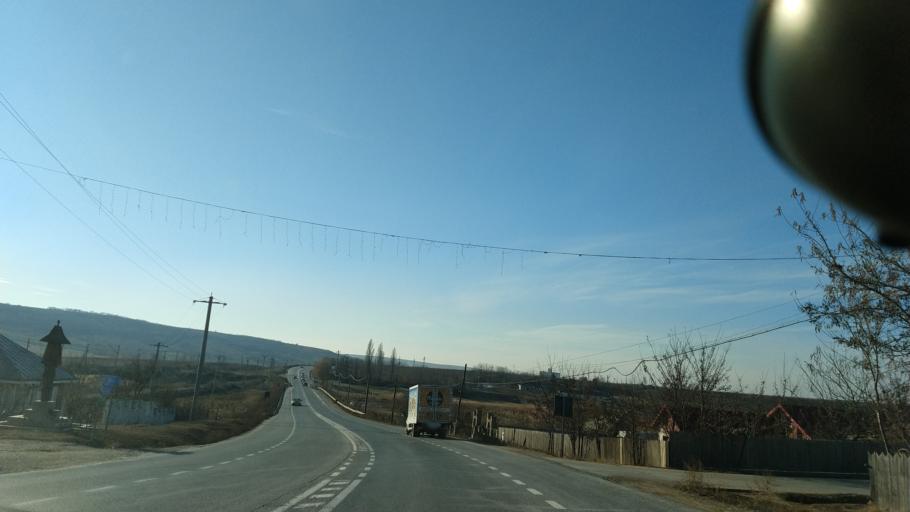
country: RO
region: Iasi
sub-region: Comuna Baltati
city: Baltati
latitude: 47.2253
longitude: 27.1813
